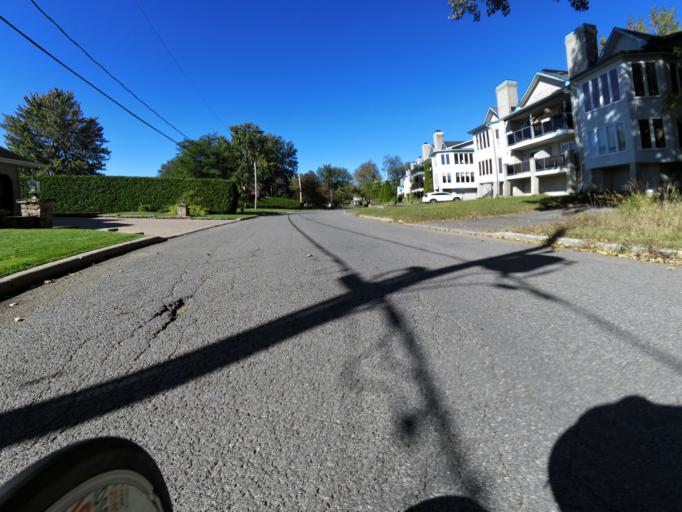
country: CA
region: Quebec
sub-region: Outaouais
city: Gatineau
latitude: 45.4762
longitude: -75.6167
